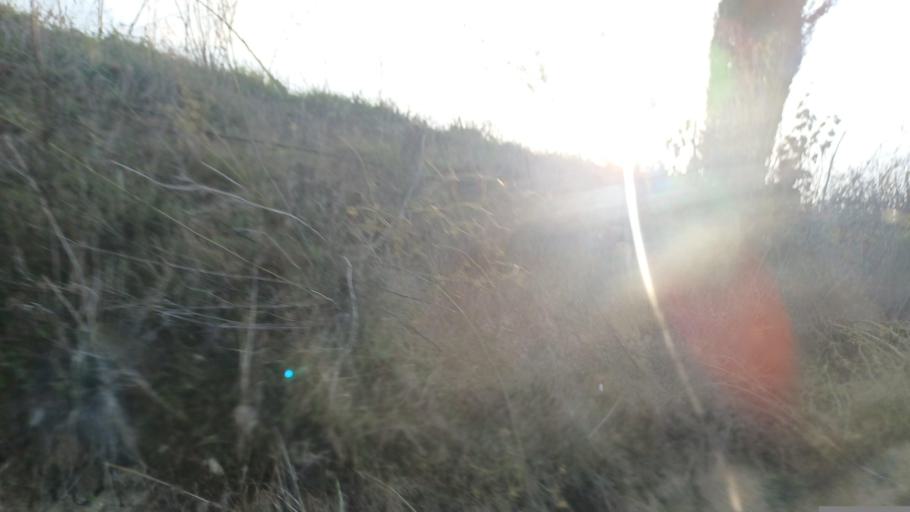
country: CY
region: Pafos
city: Tala
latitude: 34.9030
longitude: 32.4874
